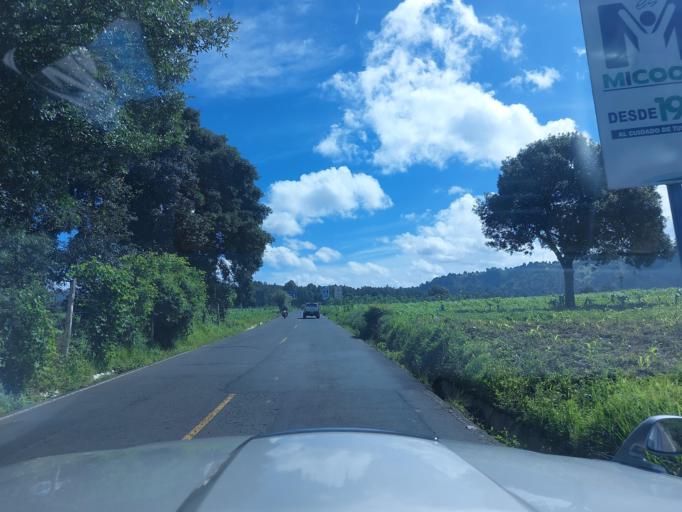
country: GT
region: Chimaltenango
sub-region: Municipio de Santa Cruz Balanya
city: Santa Cruz Balanya
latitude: 14.7017
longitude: -90.8984
